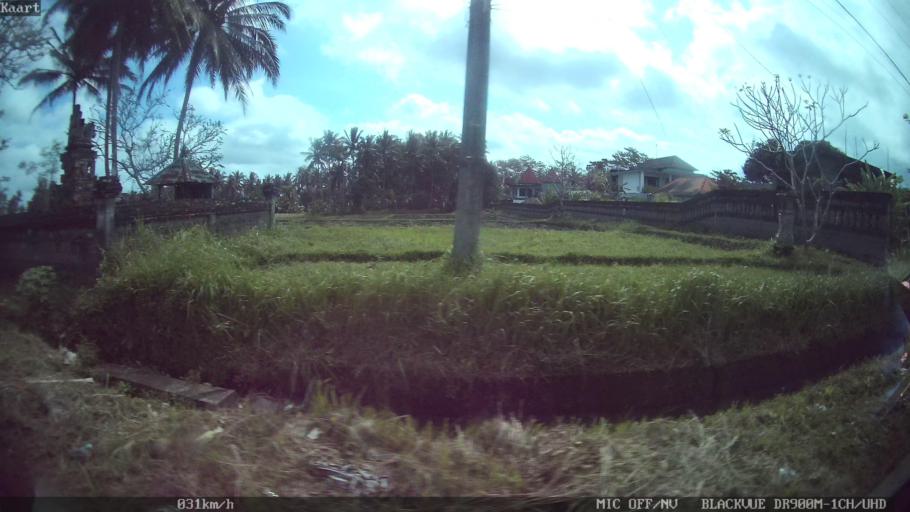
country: ID
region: Bali
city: Banjar Pesalakan
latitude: -8.5157
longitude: 115.3020
